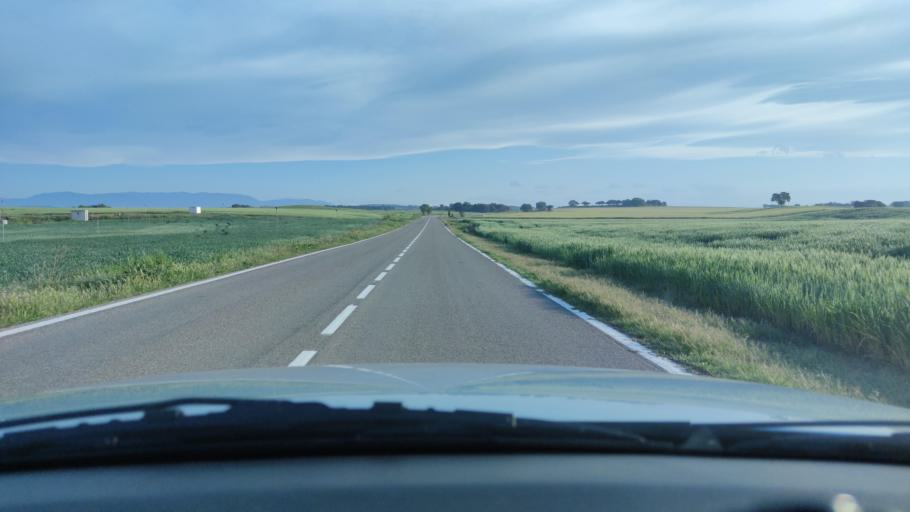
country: ES
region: Catalonia
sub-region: Provincia de Lleida
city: Agramunt
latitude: 41.8089
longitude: 1.0529
